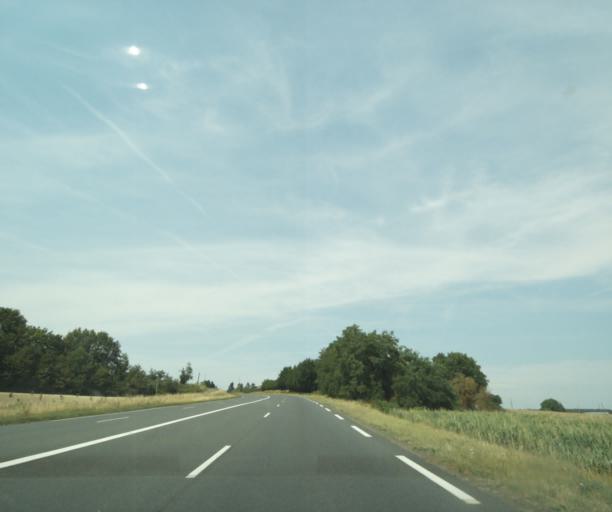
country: FR
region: Centre
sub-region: Departement d'Indre-et-Loire
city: La Celle-Saint-Avant
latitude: 47.0568
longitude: 0.6159
